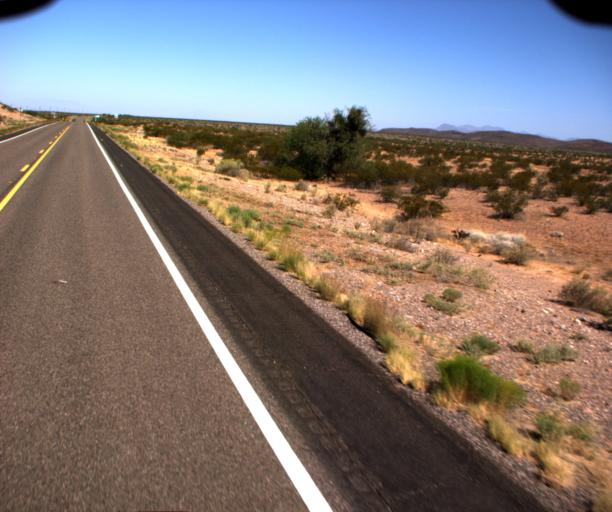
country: US
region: Arizona
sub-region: Graham County
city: Swift Trail Junction
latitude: 32.7526
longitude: -109.4106
